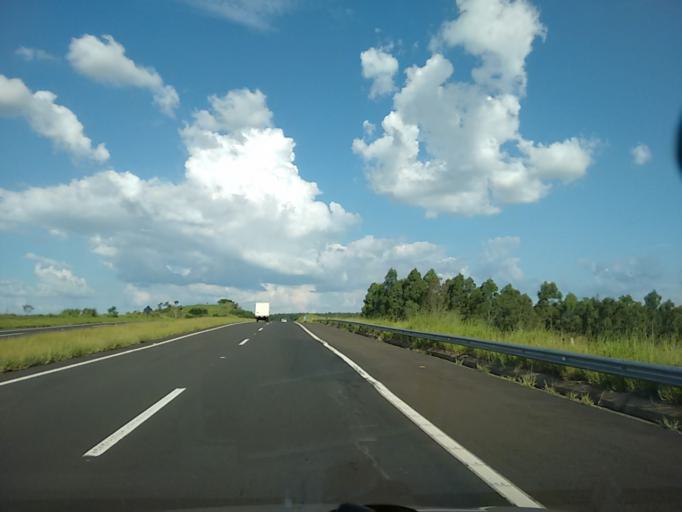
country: BR
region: Sao Paulo
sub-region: Duartina
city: Duartina
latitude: -22.3190
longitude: -49.4880
